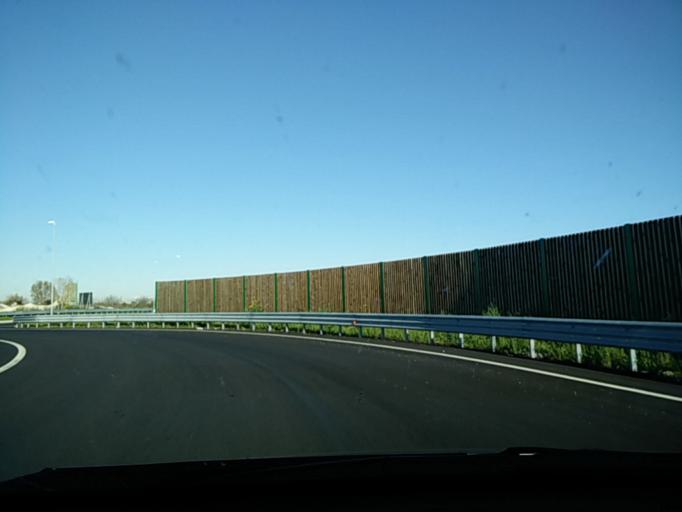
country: IT
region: Veneto
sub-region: Provincia di Venezia
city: Marcon-Gaggio-Colmello
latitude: 45.5492
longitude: 12.2970
